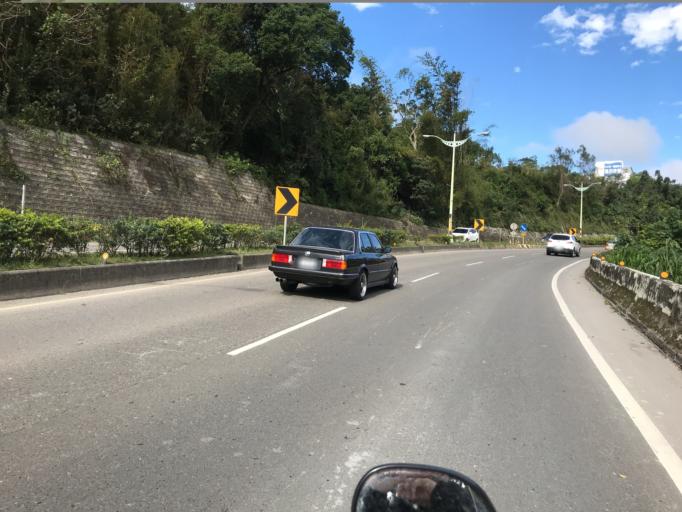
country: TW
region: Taiwan
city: Daxi
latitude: 24.8447
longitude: 121.2441
